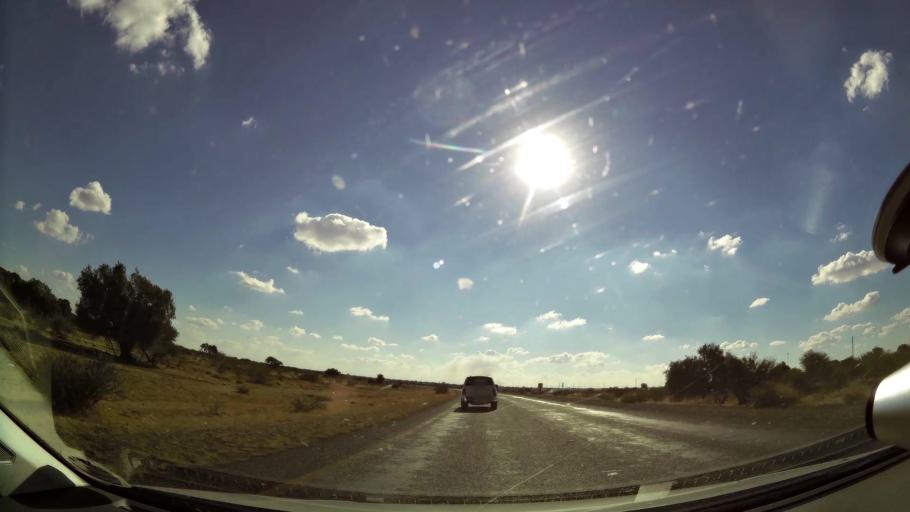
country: ZA
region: Northern Cape
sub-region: Frances Baard District Municipality
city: Kimberley
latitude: -28.7886
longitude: 24.7824
